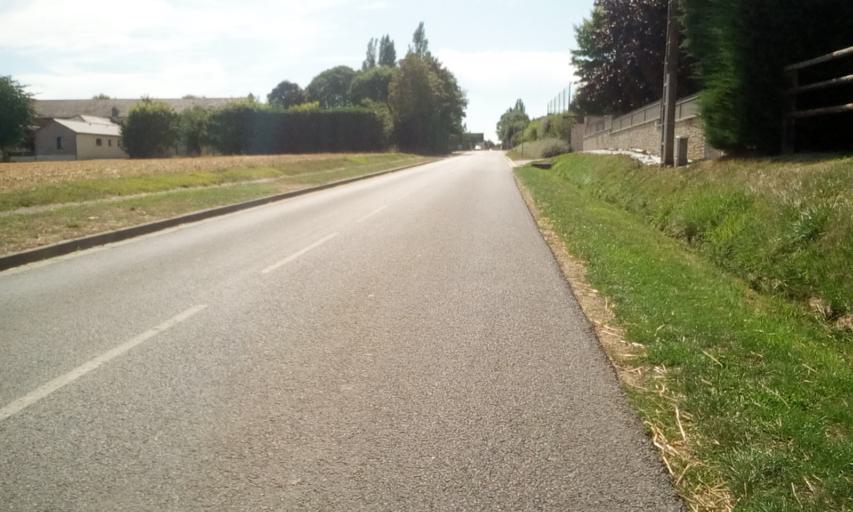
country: FR
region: Lower Normandy
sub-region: Departement du Calvados
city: Eterville
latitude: 49.1333
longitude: -0.4150
